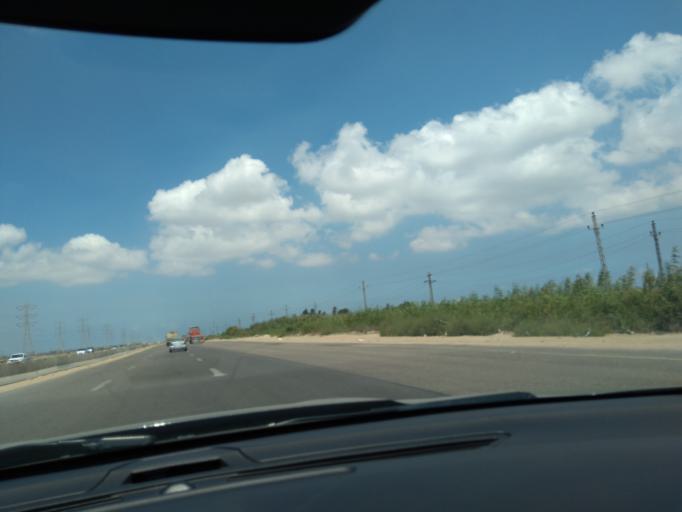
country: EG
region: Muhafazat Bur Sa`id
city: Port Said
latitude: 31.1711
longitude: 32.3015
